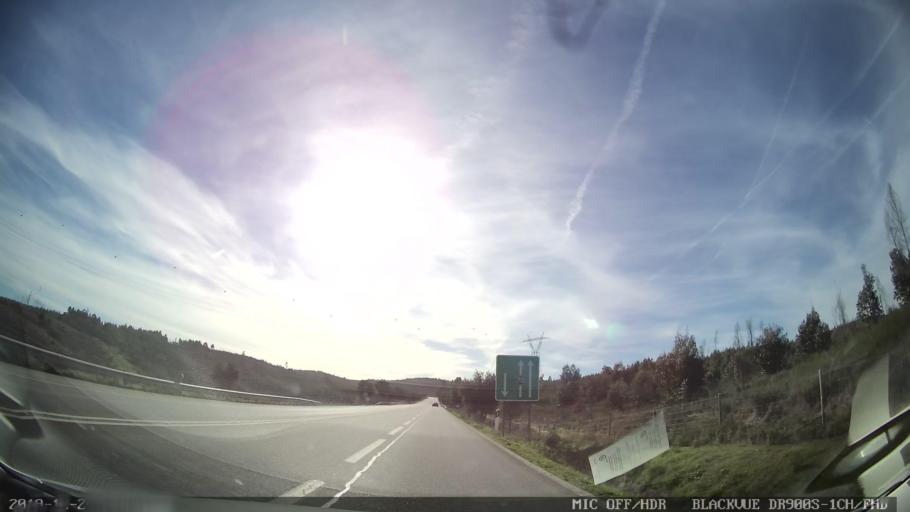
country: PT
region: Portalegre
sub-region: Nisa
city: Nisa
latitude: 39.5128
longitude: -7.7688
